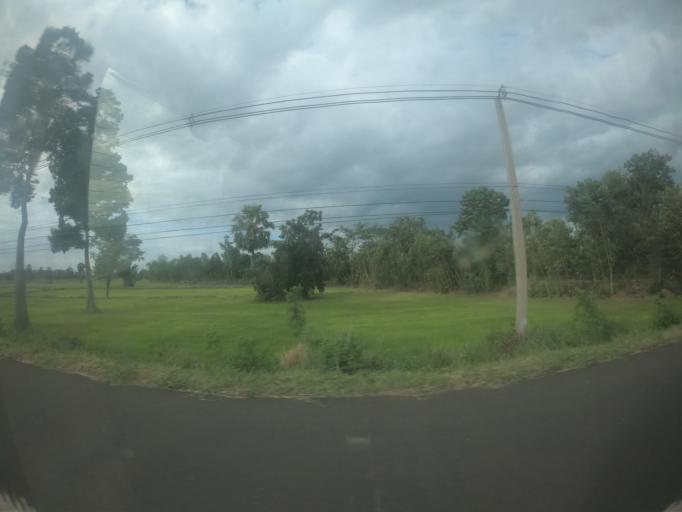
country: TH
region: Surin
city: Kap Choeng
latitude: 14.5333
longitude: 103.5282
